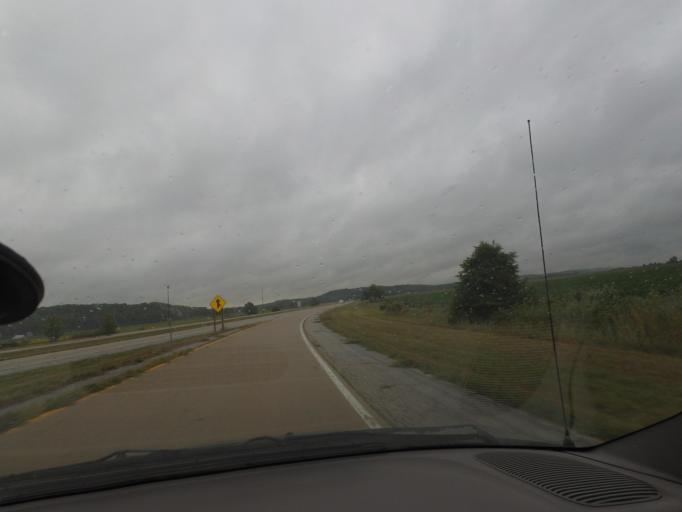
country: US
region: Illinois
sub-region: Adams County
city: Payson
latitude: 39.7180
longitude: -91.1917
